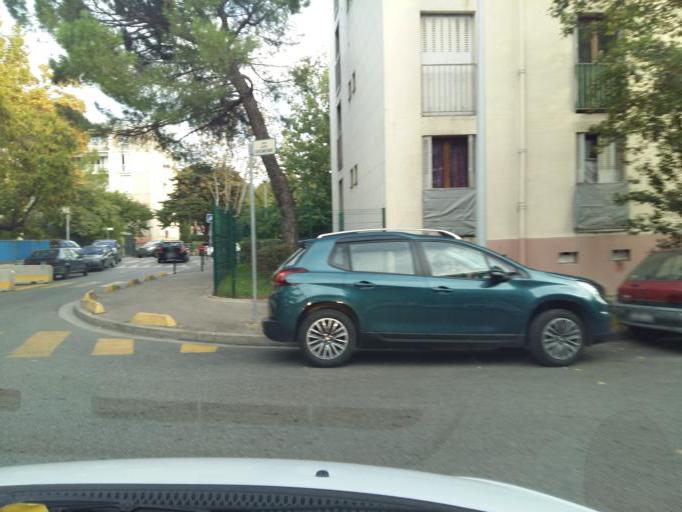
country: FR
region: Provence-Alpes-Cote d'Azur
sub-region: Departement des Bouches-du-Rhone
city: Aix-en-Provence
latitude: 43.5217
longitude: 5.4343
